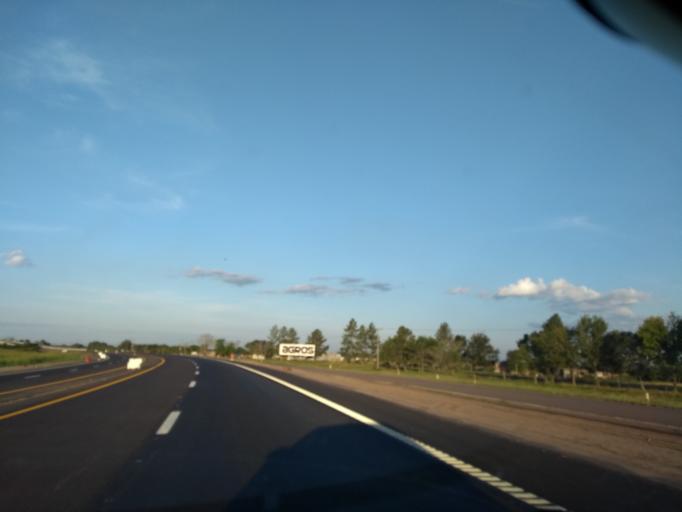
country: AR
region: Chaco
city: Makalle
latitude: -27.1942
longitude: -59.3158
